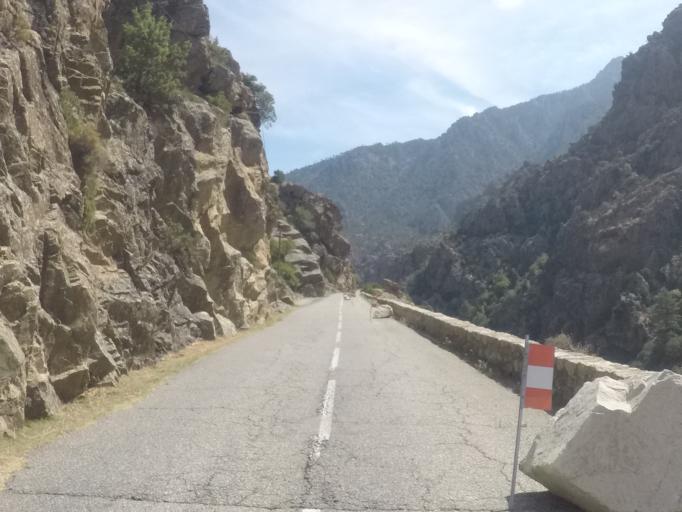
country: FR
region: Corsica
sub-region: Departement de la Haute-Corse
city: Corte
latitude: 42.3746
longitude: 9.0969
